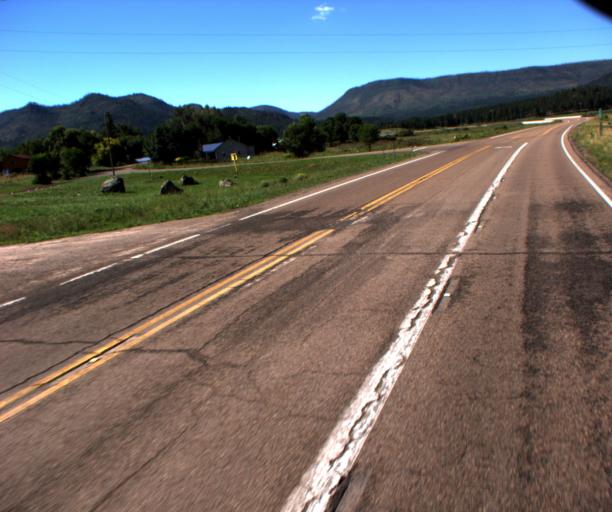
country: US
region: Arizona
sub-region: Apache County
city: Eagar
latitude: 33.9579
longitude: -109.2090
